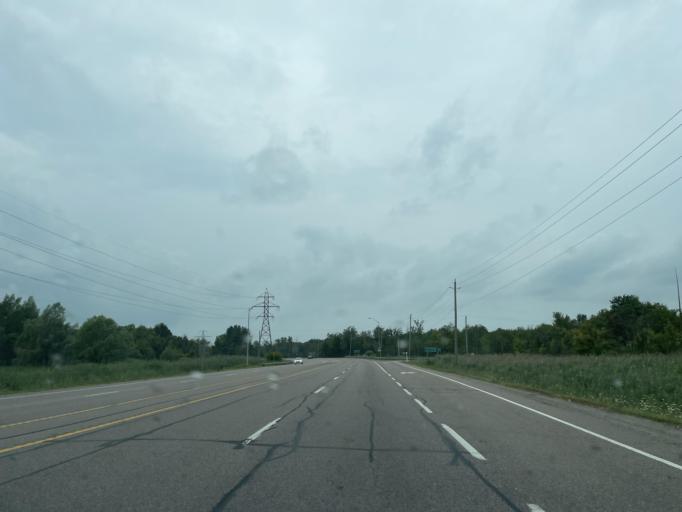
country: CA
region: Ontario
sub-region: Halton
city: Milton
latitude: 43.4079
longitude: -80.0469
